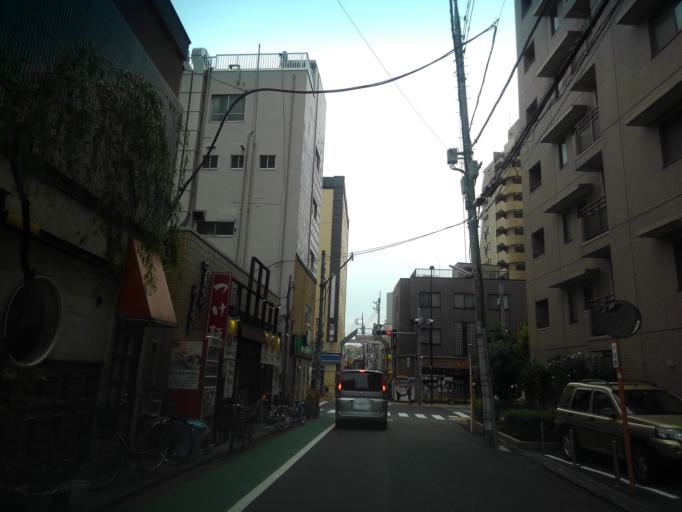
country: JP
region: Tokyo
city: Hino
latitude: 35.7024
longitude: 139.4156
